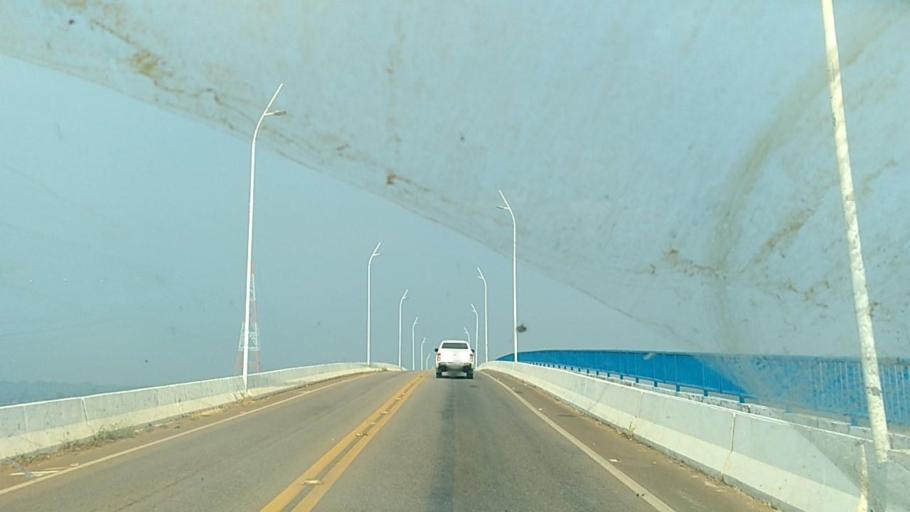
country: BR
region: Rondonia
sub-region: Porto Velho
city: Porto Velho
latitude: -8.7390
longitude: -63.9227
